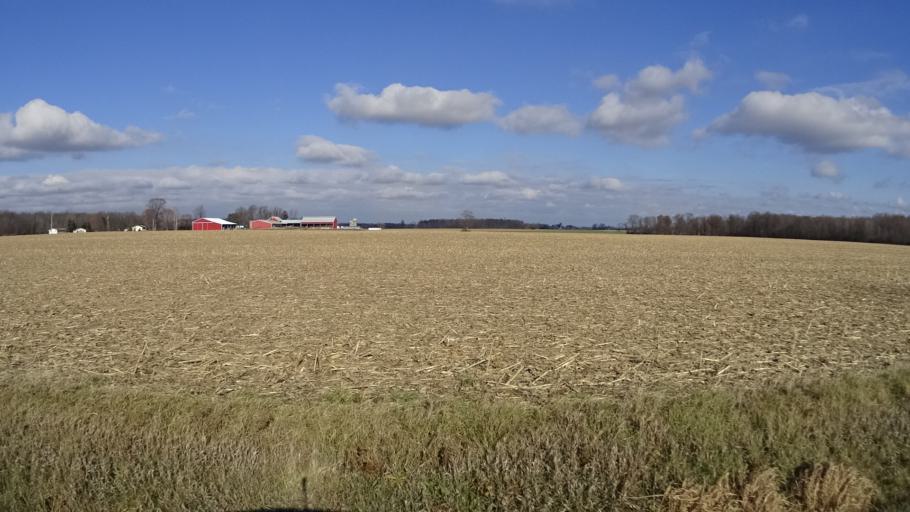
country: US
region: Ohio
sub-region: Lorain County
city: Camden
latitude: 41.2375
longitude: -82.2868
